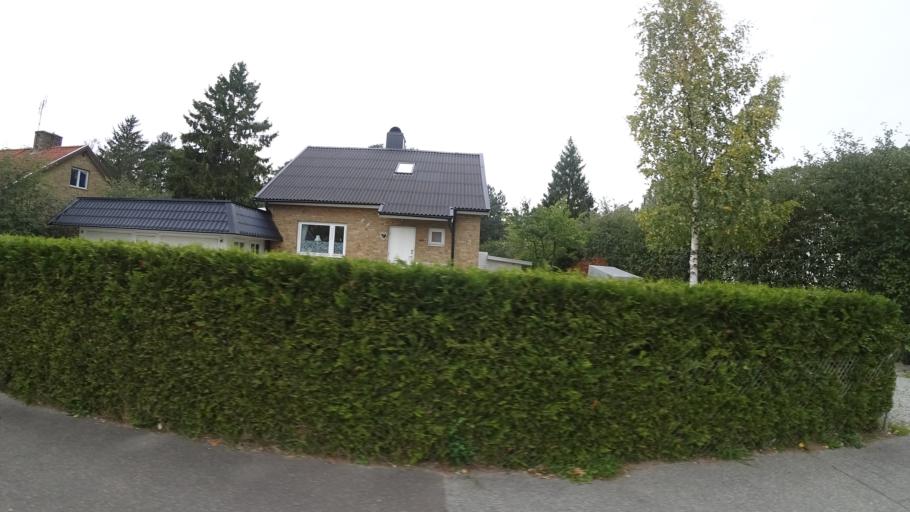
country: SE
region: Skane
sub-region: Kavlinge Kommun
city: Kaevlinge
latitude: 55.7741
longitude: 13.0867
